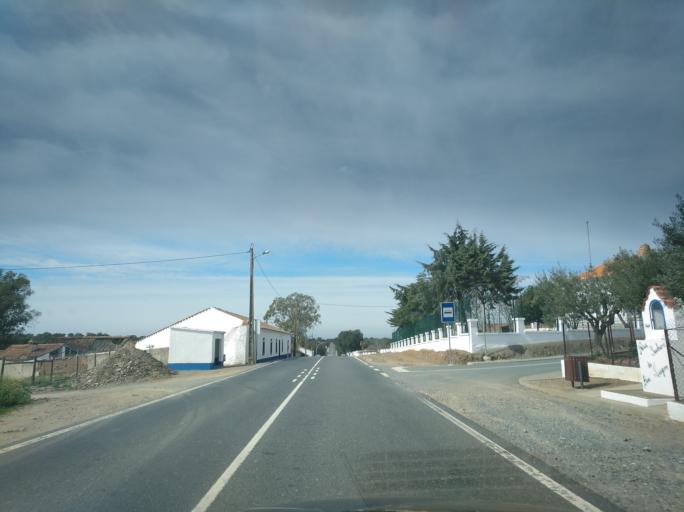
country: PT
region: Beja
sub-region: Mertola
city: Mertola
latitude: 37.7438
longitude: -7.7934
